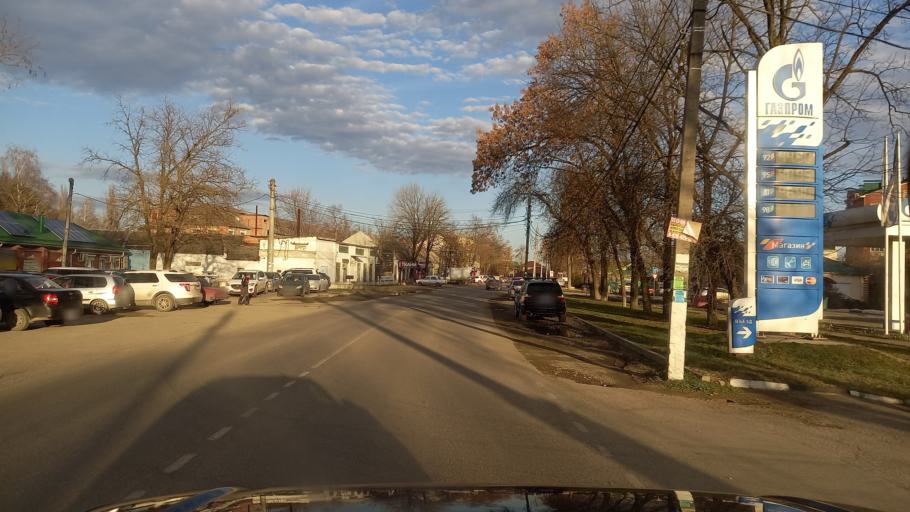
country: RU
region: Krasnodarskiy
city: Pashkovskiy
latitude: 45.0149
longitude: 39.1042
